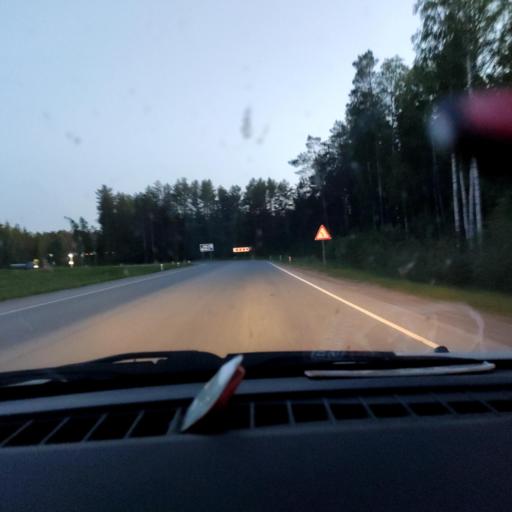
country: RU
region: Perm
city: Overyata
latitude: 58.0426
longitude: 55.8705
